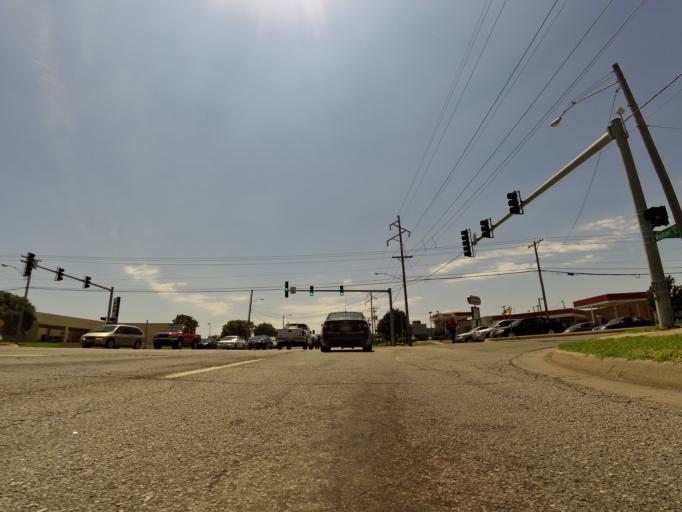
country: US
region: Kansas
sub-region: Sedgwick County
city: Bellaire
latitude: 37.7233
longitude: -97.2624
